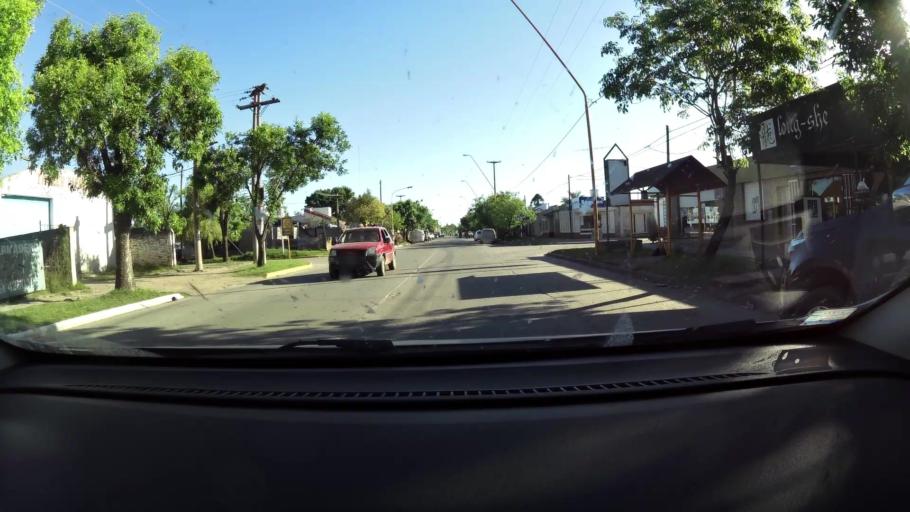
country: AR
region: Cordoba
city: San Francisco
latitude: -31.4364
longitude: -62.0679
